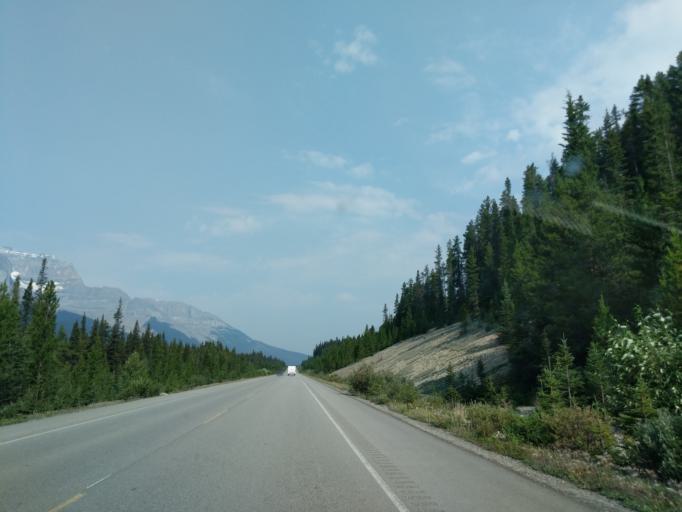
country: CA
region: Alberta
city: Lake Louise
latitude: 51.8647
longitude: -116.6637
